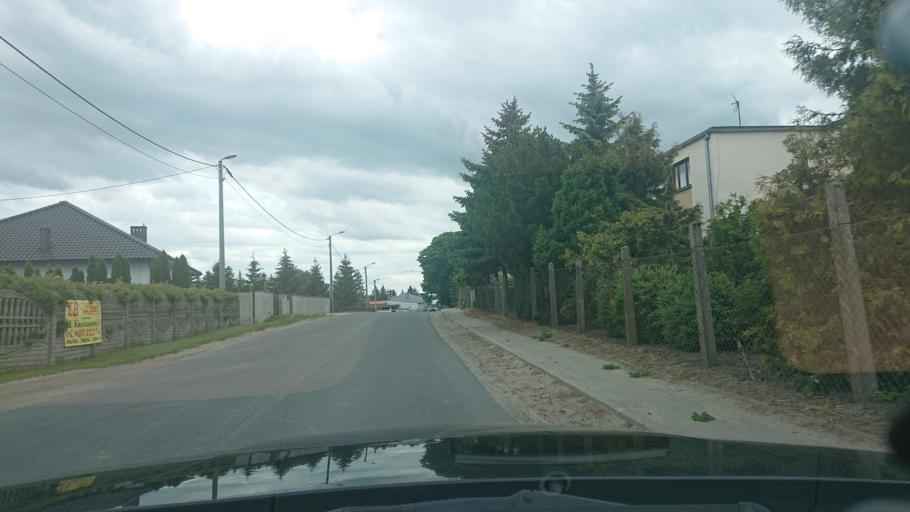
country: PL
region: Greater Poland Voivodeship
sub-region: Powiat gnieznienski
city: Gniezno
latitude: 52.5413
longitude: 17.5405
